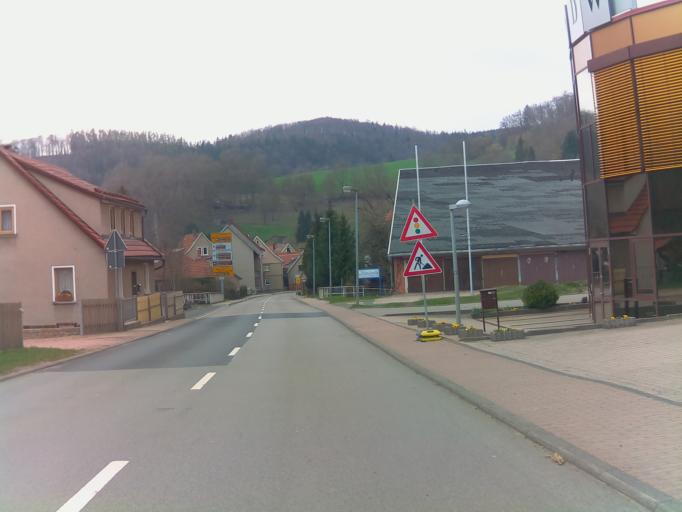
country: DE
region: Thuringia
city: Pappenheim
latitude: 50.7531
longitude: 10.5047
